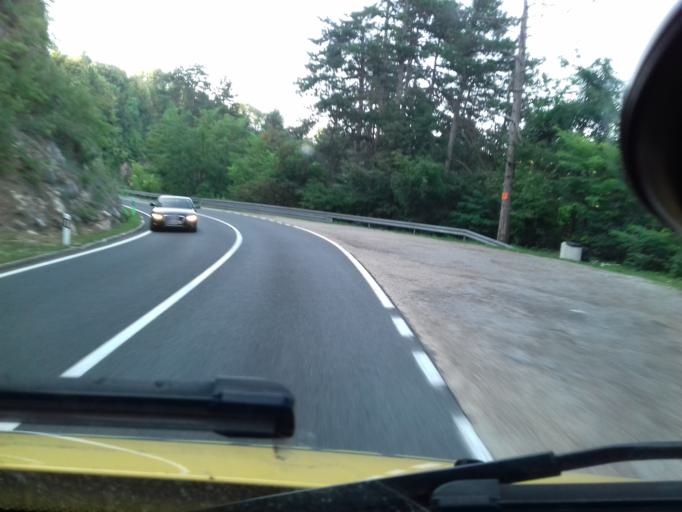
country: BA
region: Federation of Bosnia and Herzegovina
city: Ostrozac
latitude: 44.9008
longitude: 15.9307
